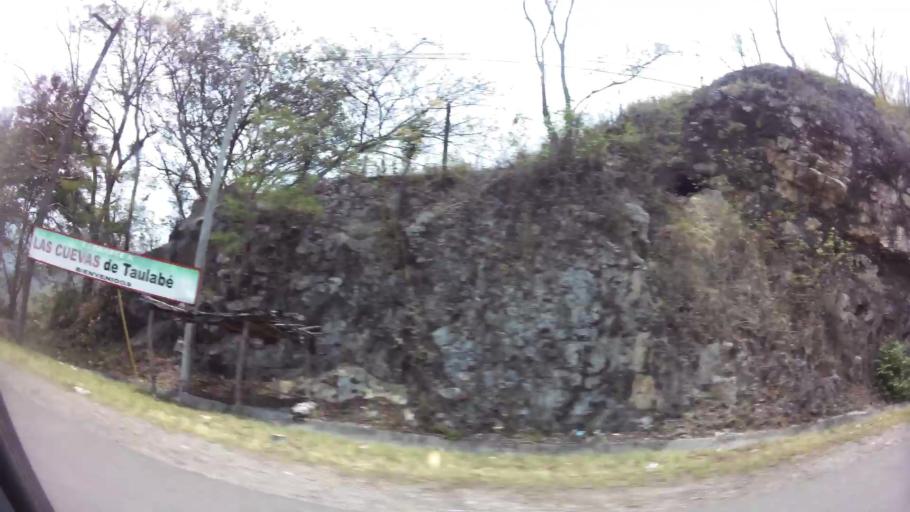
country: HN
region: Comayagua
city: Taulabe
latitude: 14.6951
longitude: -87.9516
